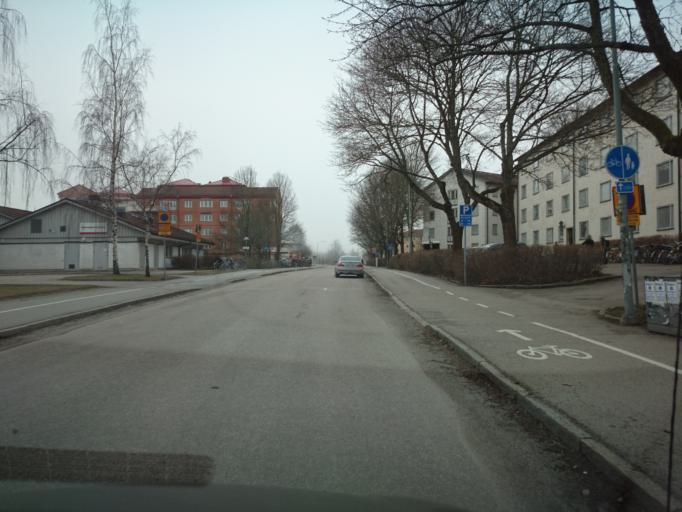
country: SE
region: Uppsala
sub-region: Uppsala Kommun
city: Uppsala
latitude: 59.8573
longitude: 17.6193
